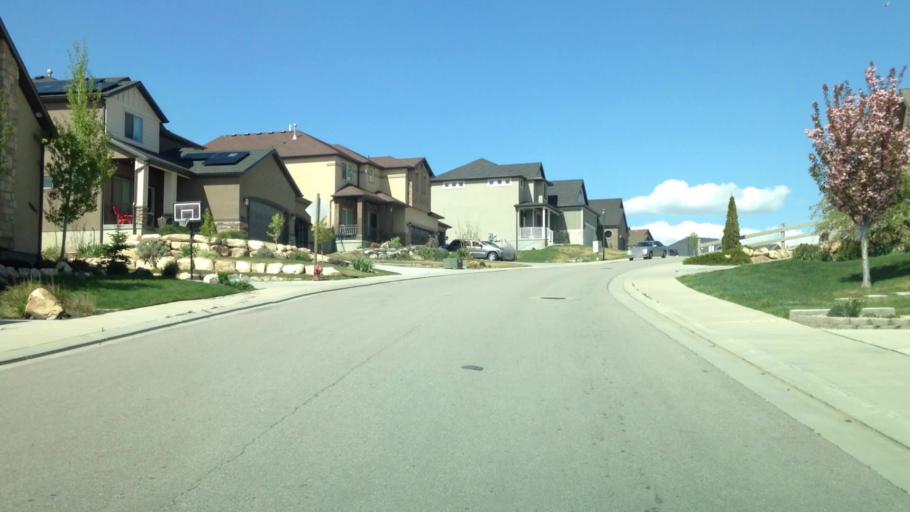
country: US
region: Utah
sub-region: Utah County
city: Saratoga Springs
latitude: 40.3777
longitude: -111.9677
